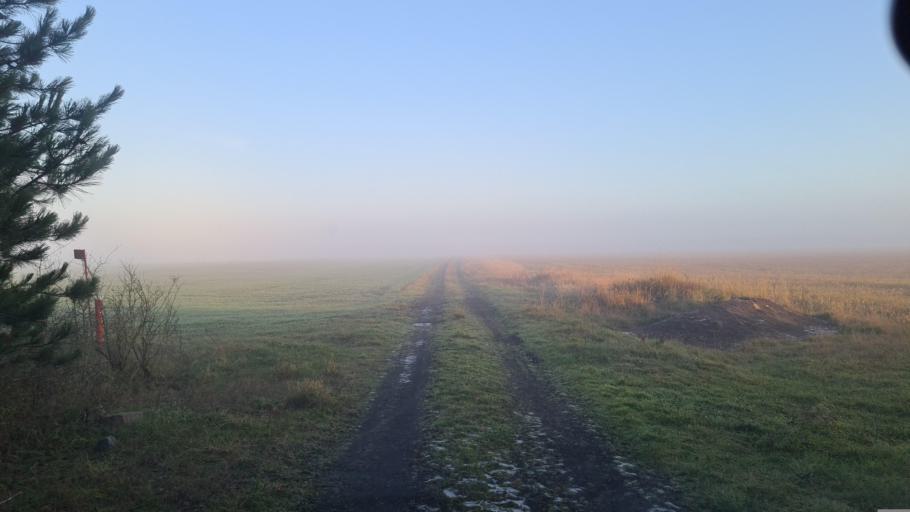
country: DE
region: Brandenburg
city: Lauchhammer
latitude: 51.5509
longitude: 13.7587
